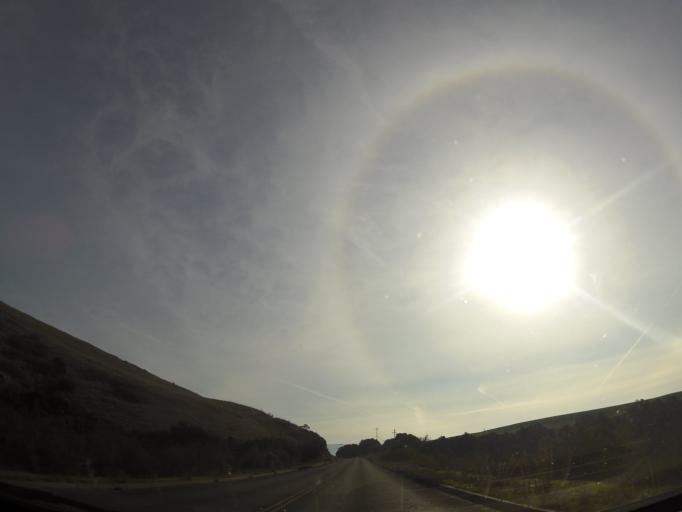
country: US
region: California
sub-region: Monterey County
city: Prunedale
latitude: 36.8076
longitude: -121.6217
